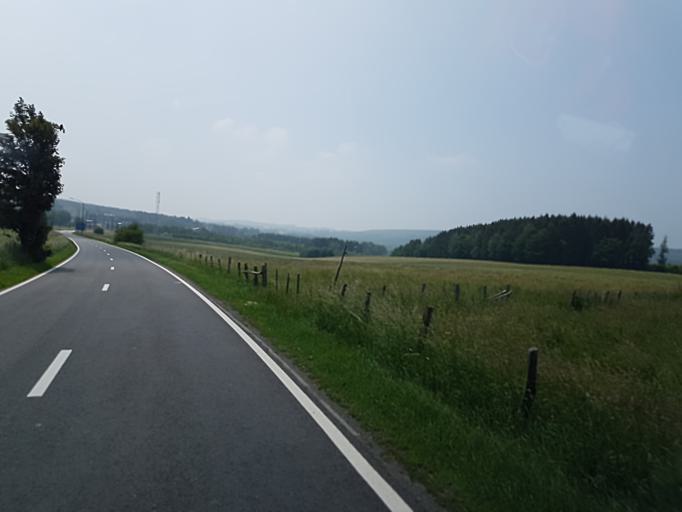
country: BE
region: Wallonia
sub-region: Province du Luxembourg
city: Manhay
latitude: 50.3107
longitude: 5.7203
